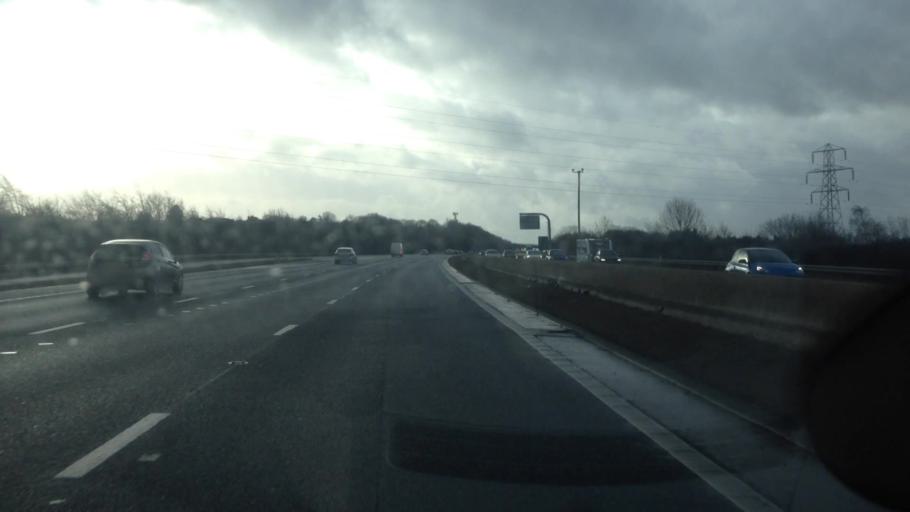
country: GB
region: England
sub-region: City and Borough of Wakefield
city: Crigglestone
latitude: 53.6474
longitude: -1.5302
